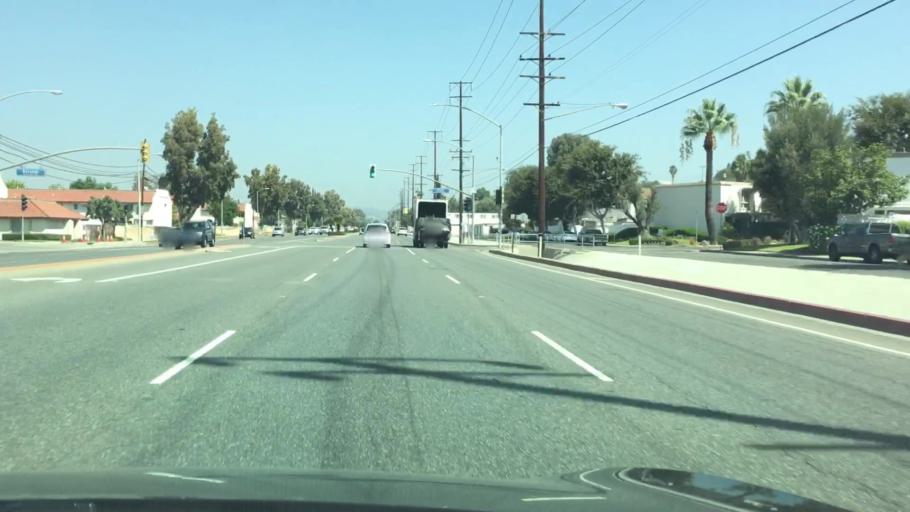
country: US
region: California
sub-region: Orange County
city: Buena Park
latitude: 33.8904
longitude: -117.9913
